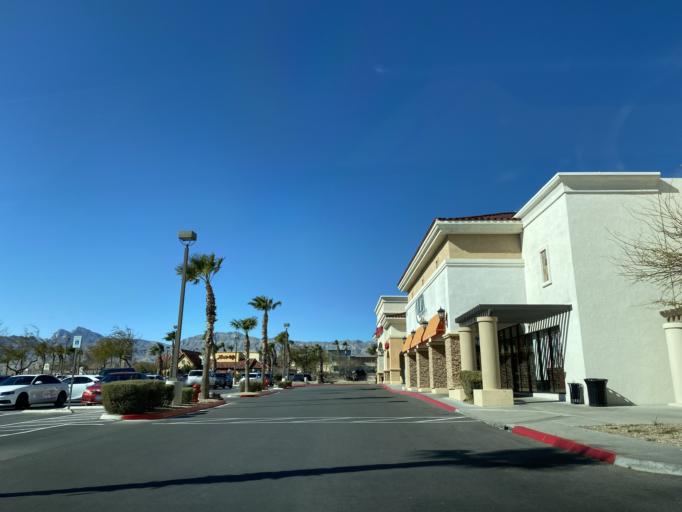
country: US
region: Nevada
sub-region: Clark County
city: Summerlin South
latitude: 36.2833
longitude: -115.2859
